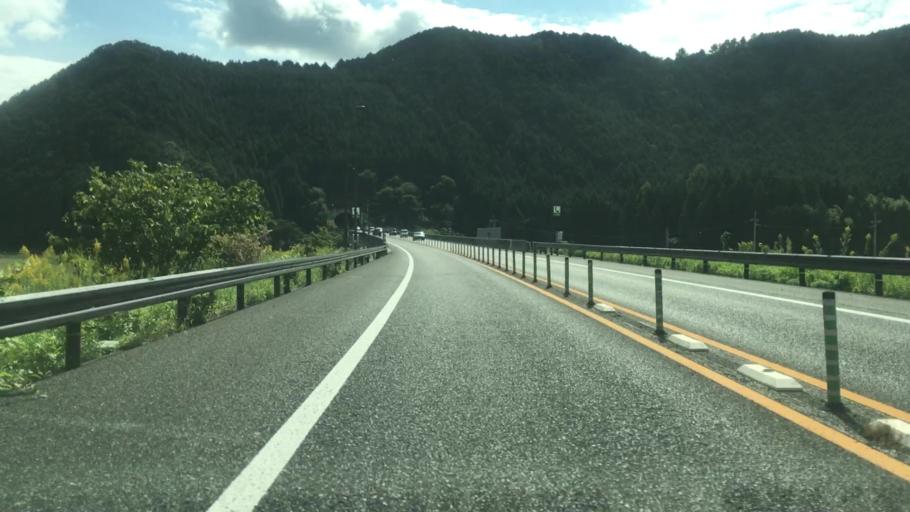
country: JP
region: Kyoto
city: Fukuchiyama
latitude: 35.2309
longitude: 135.0229
